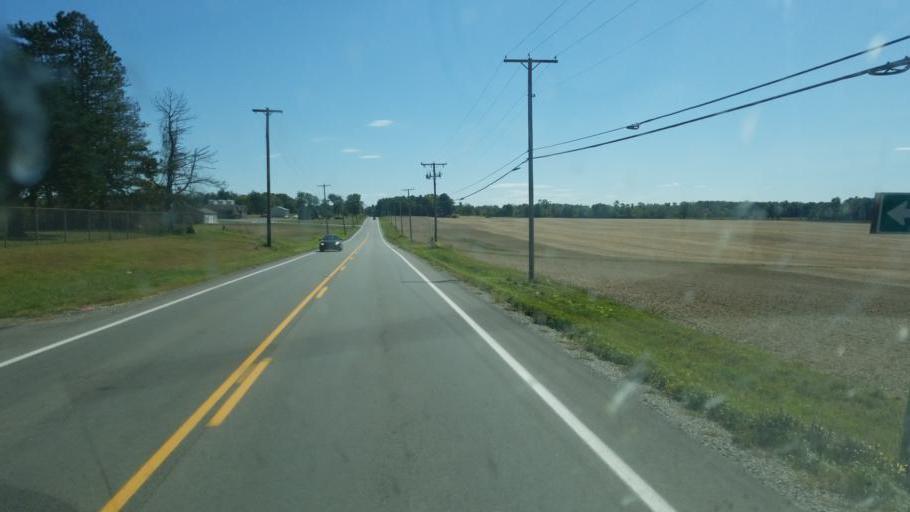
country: US
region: Ohio
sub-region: Huron County
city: Plymouth
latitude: 41.0158
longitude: -82.6754
